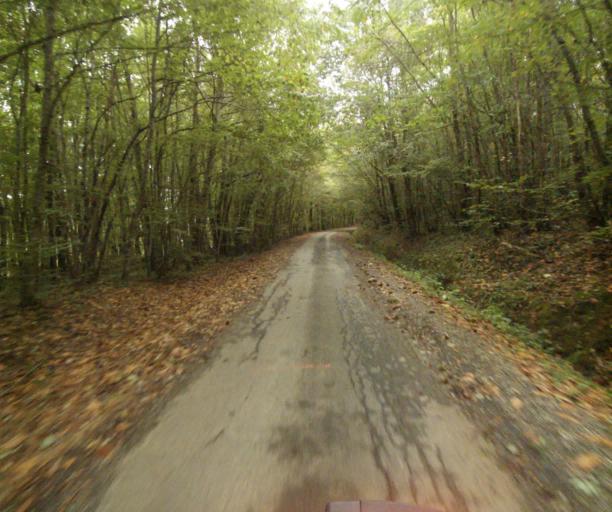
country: FR
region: Midi-Pyrenees
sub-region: Departement du Tarn-et-Garonne
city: Nohic
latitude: 43.9128
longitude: 1.4645
